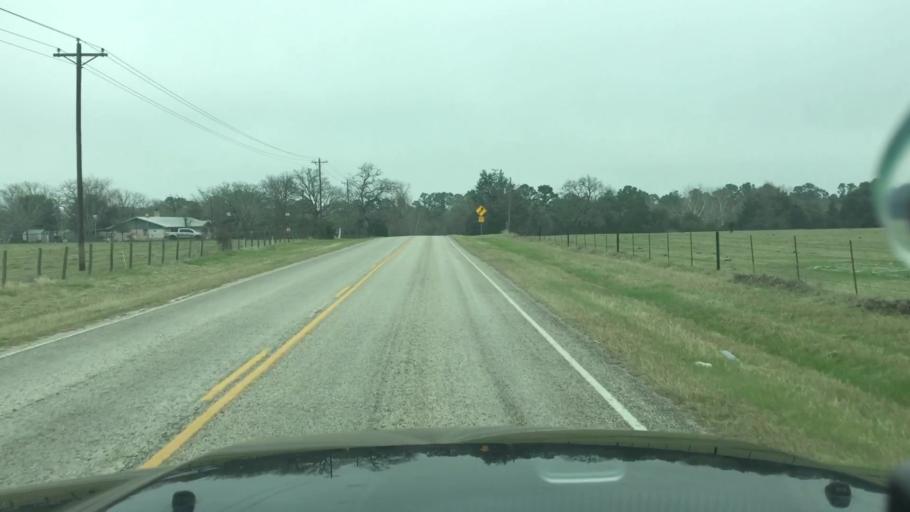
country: US
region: Texas
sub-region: Fayette County
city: La Grange
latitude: 30.0031
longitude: -96.8998
